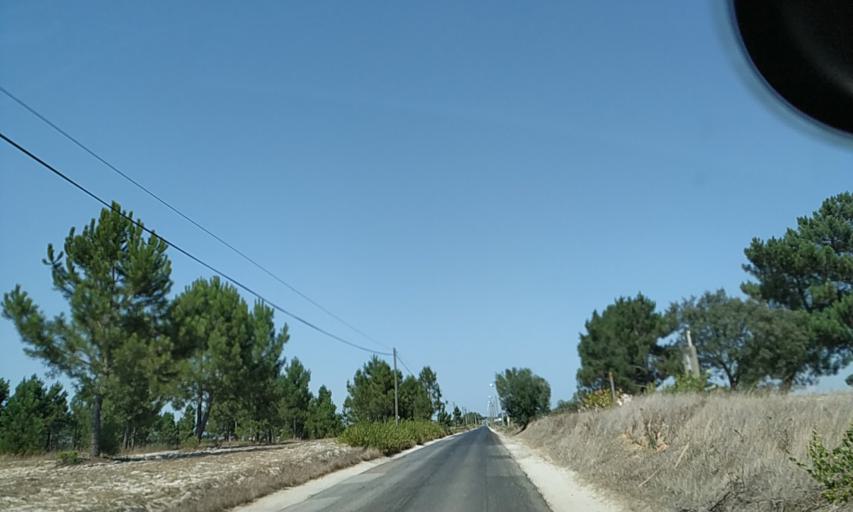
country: PT
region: Santarem
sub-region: Benavente
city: Poceirao
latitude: 38.6919
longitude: -8.7294
